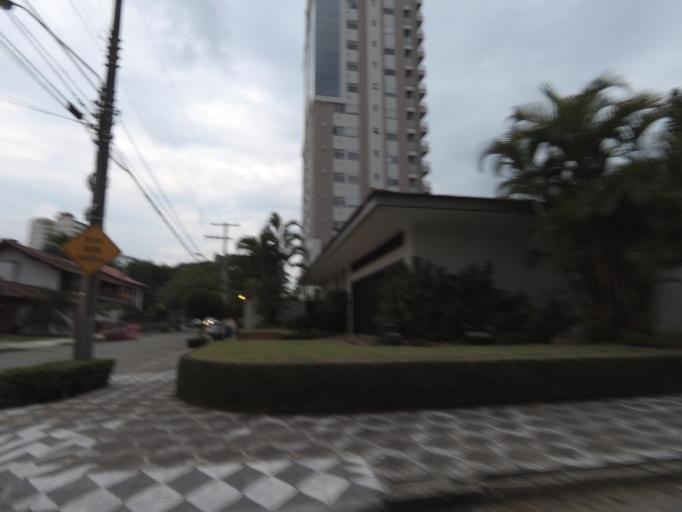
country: BR
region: Santa Catarina
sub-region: Blumenau
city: Blumenau
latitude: -26.9174
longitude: -49.0620
